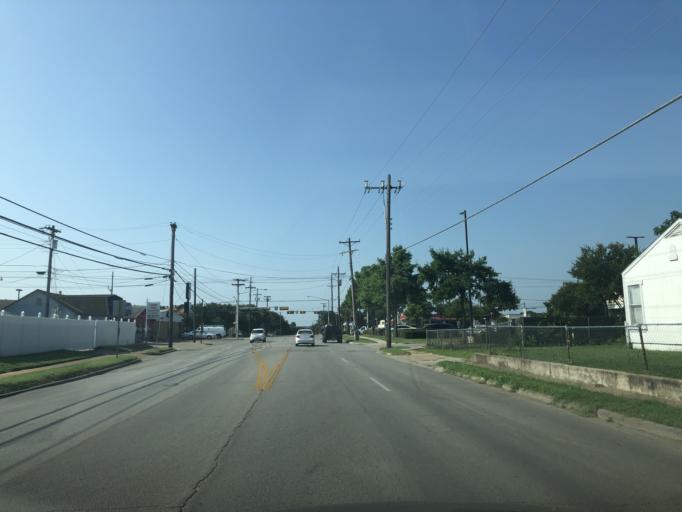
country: US
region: Texas
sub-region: Dallas County
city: Irving
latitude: 32.8015
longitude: -96.9770
